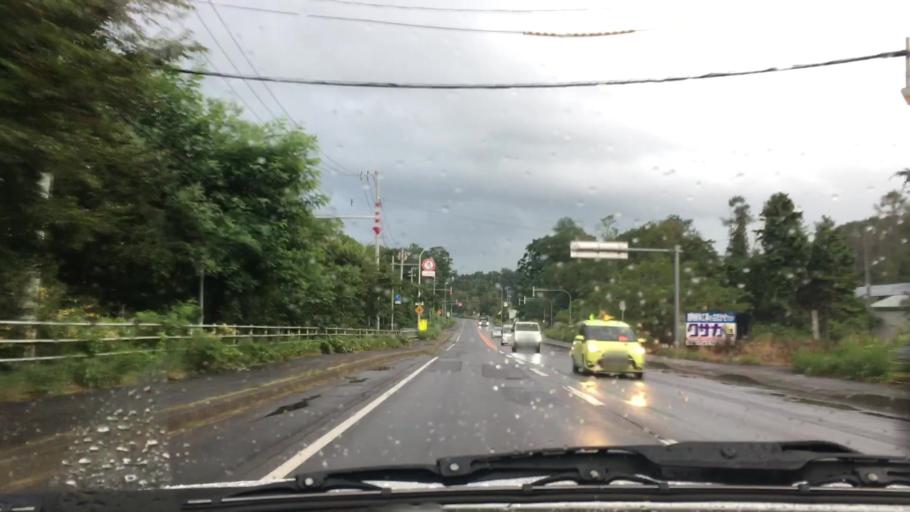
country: JP
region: Hokkaido
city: Nanae
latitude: 42.0855
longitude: 140.5845
